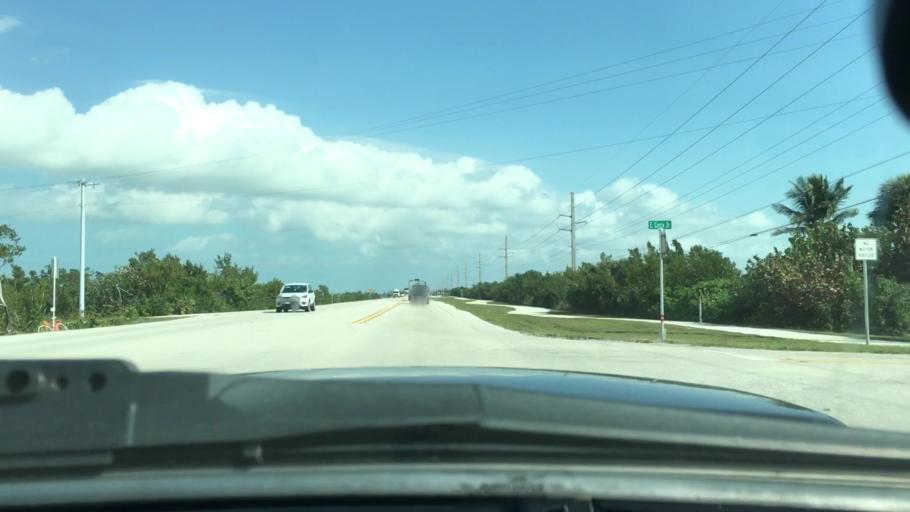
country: US
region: Florida
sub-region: Monroe County
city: Big Coppitt Key
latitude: 24.6294
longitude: -81.5925
